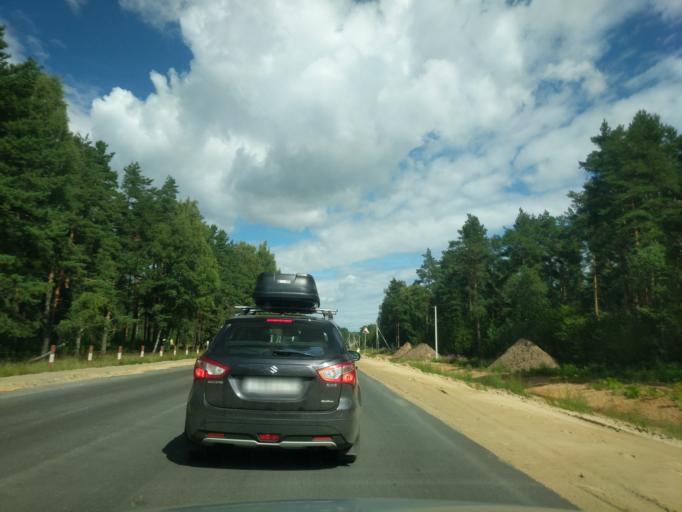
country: RU
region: Jaroslavl
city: Levashevo
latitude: 57.6687
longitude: 40.5780
